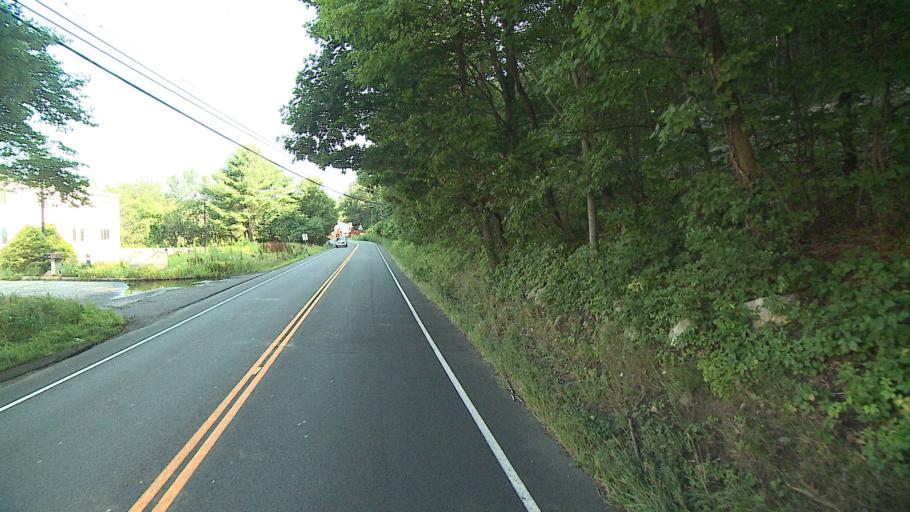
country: US
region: Connecticut
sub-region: Fairfield County
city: Georgetown
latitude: 41.2810
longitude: -73.4456
